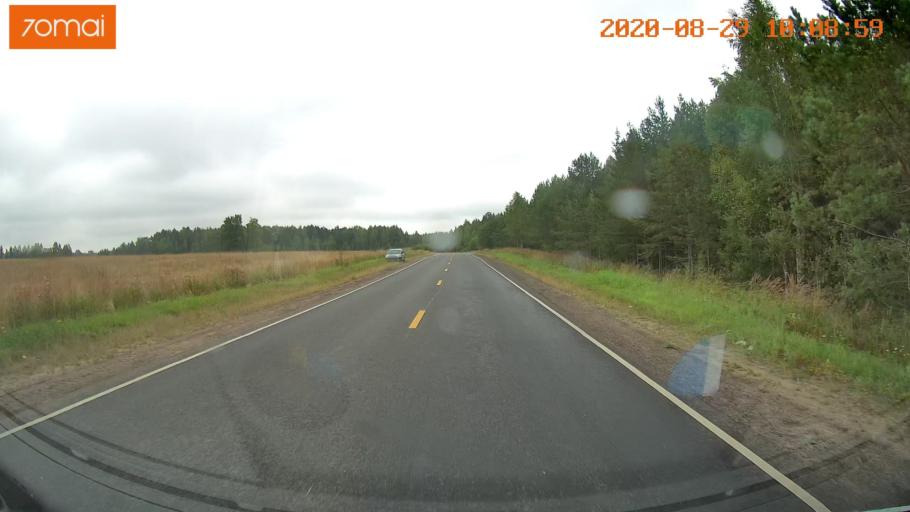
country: RU
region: Ivanovo
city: Kuznechikha
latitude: 57.3743
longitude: 42.6044
